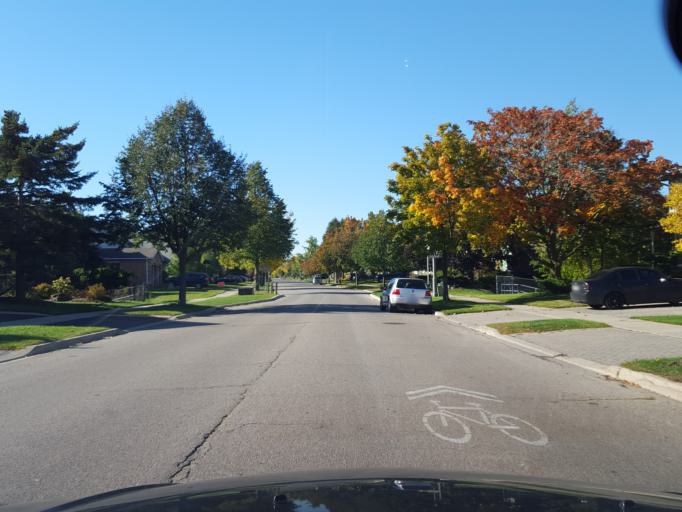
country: CA
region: Ontario
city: Burlington
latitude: 43.3882
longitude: -79.8034
